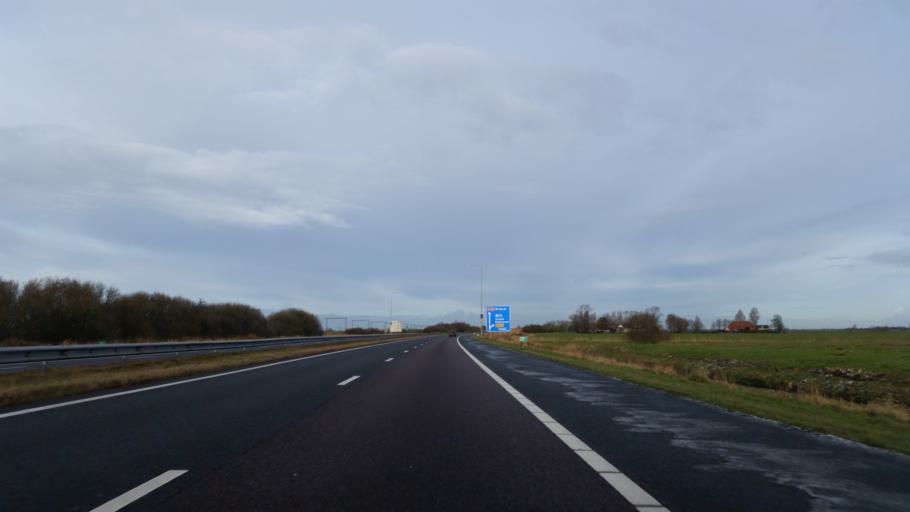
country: NL
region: Friesland
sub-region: Gemeente Boarnsterhim
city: Grou
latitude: 53.0993
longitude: 5.8189
